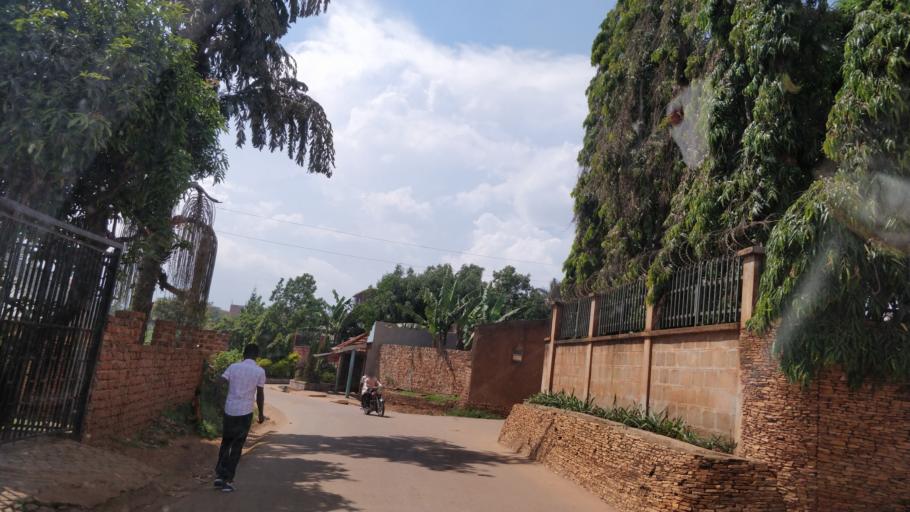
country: UG
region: Central Region
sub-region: Kampala District
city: Kampala
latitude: 0.2836
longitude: 32.6141
